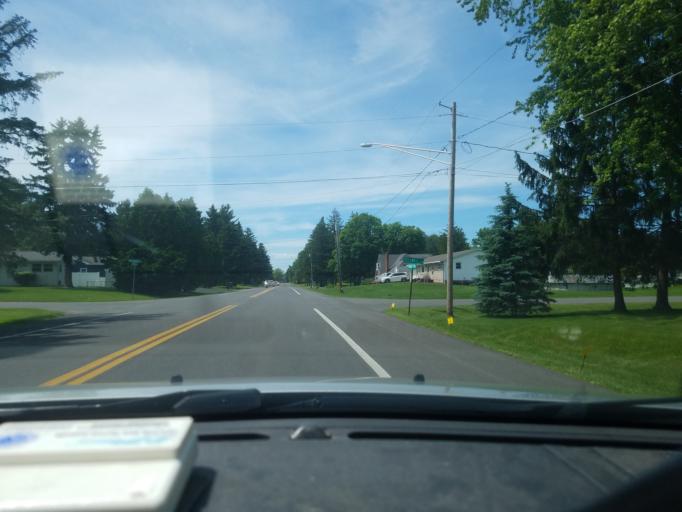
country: US
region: New York
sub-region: Onondaga County
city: East Syracuse
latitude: 43.0808
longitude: -76.0721
